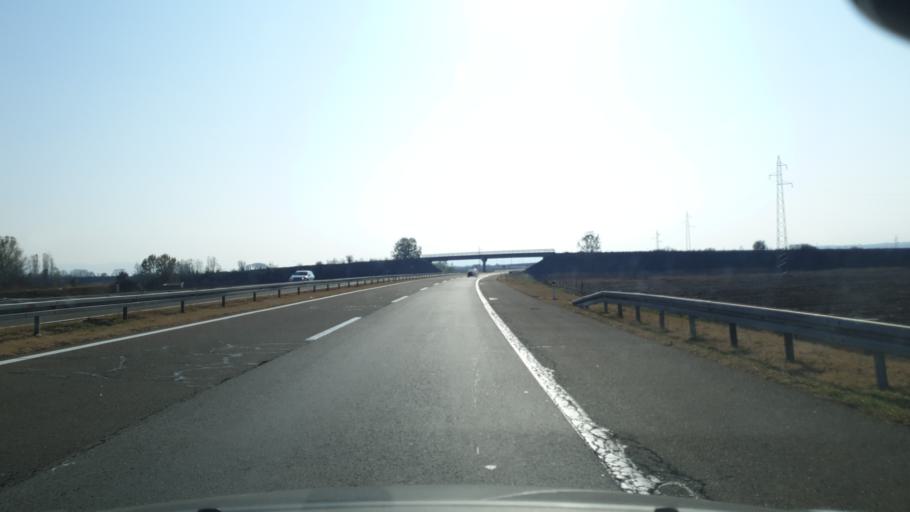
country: RS
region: Central Serbia
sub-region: Nisavski Okrug
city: Nis
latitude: 43.3359
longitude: 21.8151
